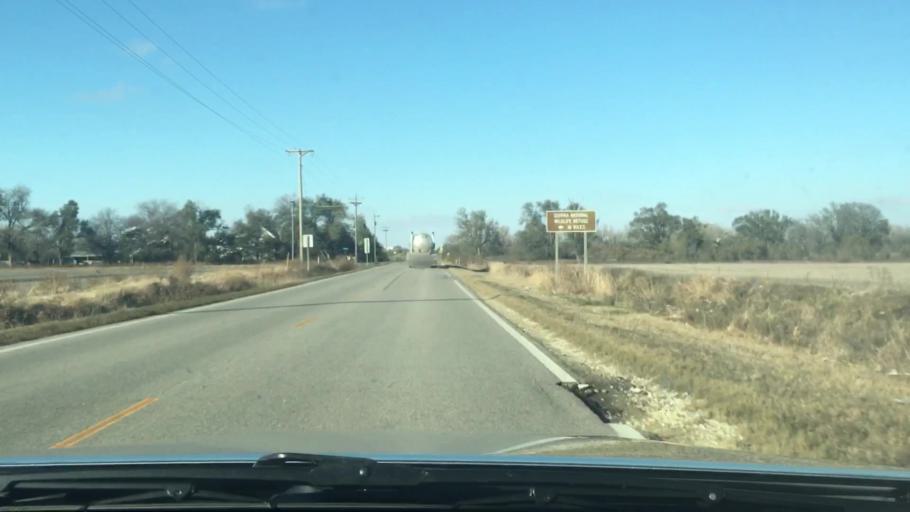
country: US
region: Kansas
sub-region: Rice County
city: Sterling
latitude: 38.1650
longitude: -98.2068
